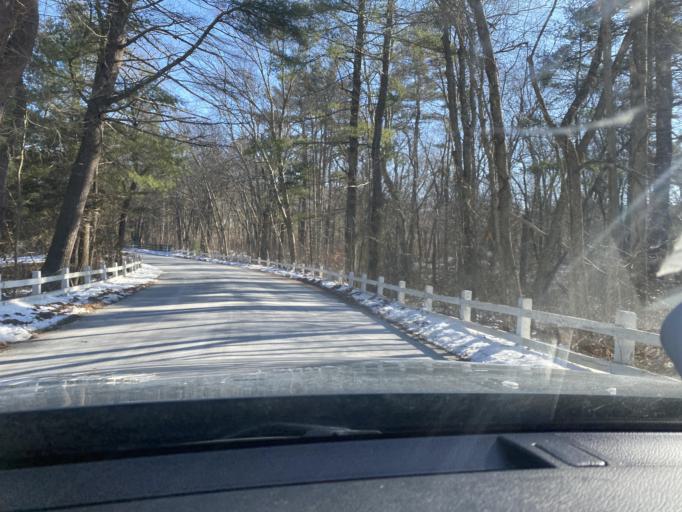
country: US
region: Massachusetts
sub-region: Norfolk County
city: Walpole
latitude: 42.1534
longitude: -71.2101
